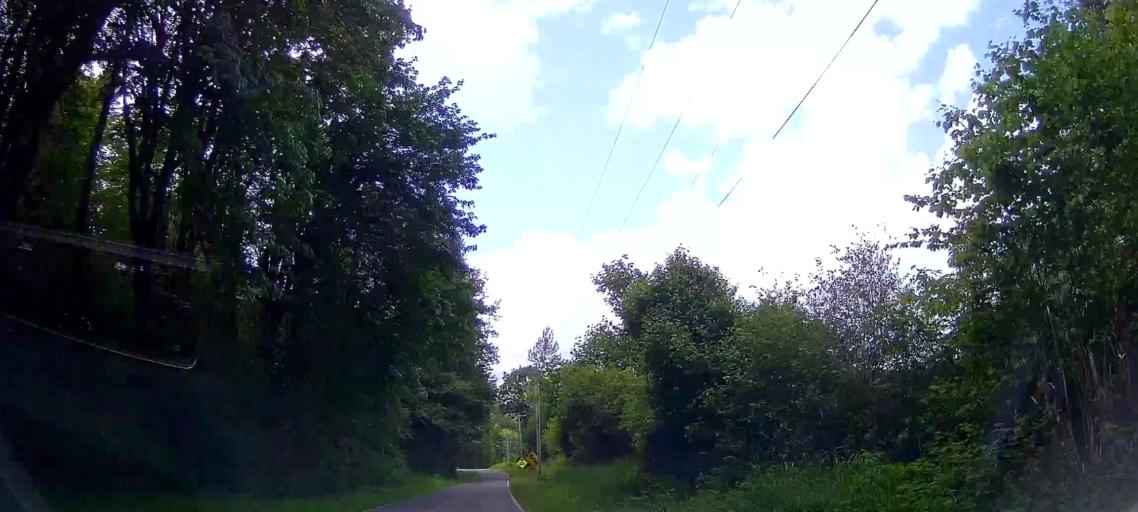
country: US
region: Washington
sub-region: Skagit County
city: Sedro-Woolley
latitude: 48.6775
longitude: -122.1614
